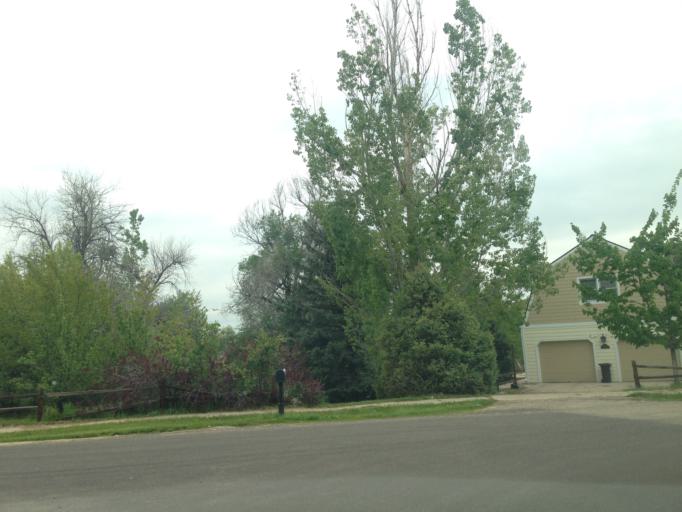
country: US
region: Colorado
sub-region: Boulder County
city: Louisville
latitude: 40.0044
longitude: -105.1716
